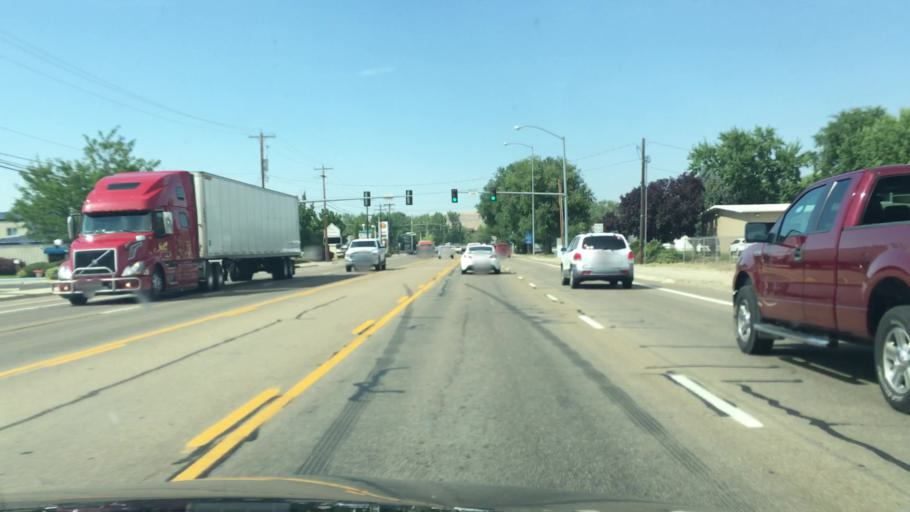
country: US
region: Idaho
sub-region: Ada County
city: Garden City
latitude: 43.6570
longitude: -116.2797
